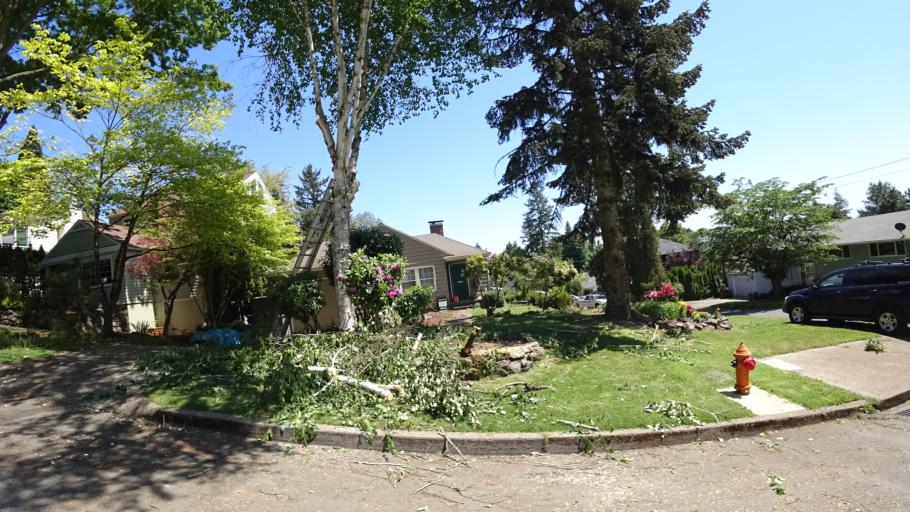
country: US
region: Oregon
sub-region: Clackamas County
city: Milwaukie
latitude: 45.4725
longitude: -122.6825
